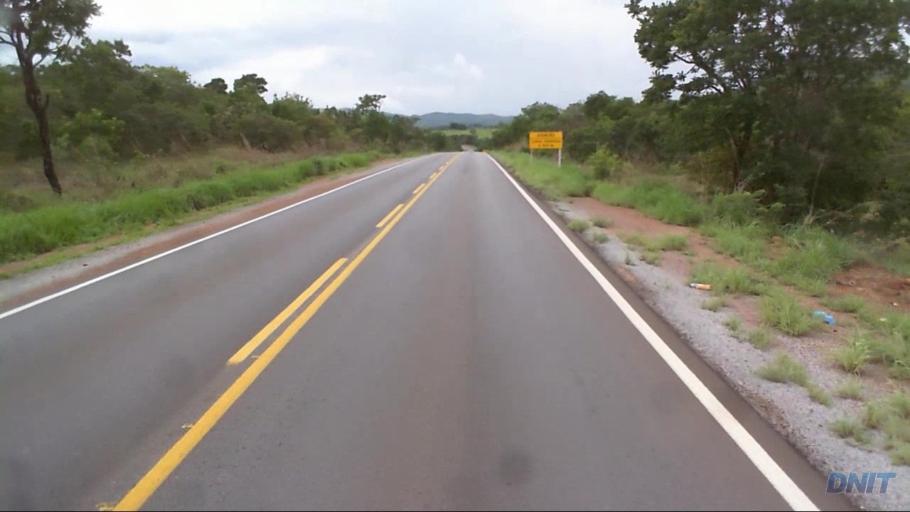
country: BR
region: Goias
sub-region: Padre Bernardo
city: Padre Bernardo
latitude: -15.4077
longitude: -48.2002
